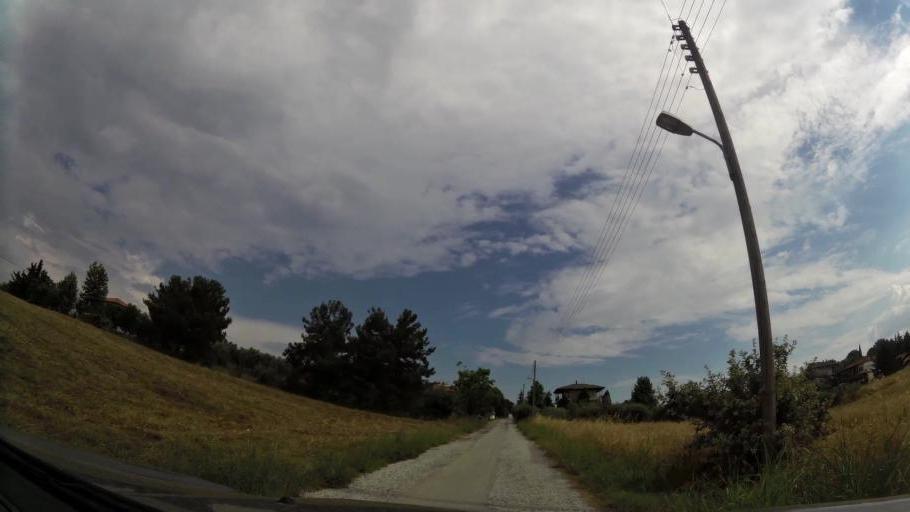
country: GR
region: Central Macedonia
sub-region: Nomos Pierias
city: Makrygialos
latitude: 40.4231
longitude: 22.6053
